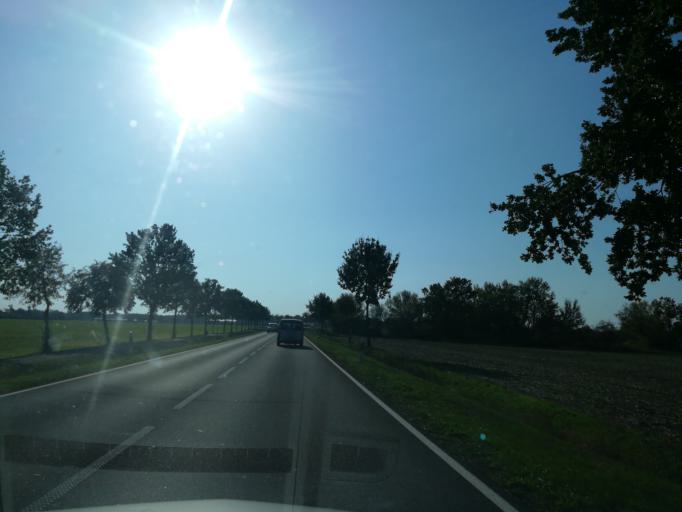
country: DE
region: Saxony-Anhalt
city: Wahlitz
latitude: 52.1289
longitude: 11.7612
